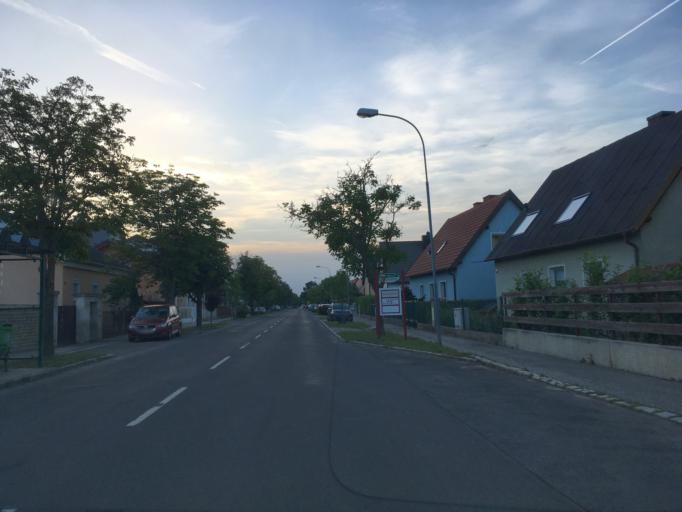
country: AT
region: Lower Austria
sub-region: Politischer Bezirk Baden
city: Teesdorf
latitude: 47.9451
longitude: 16.2877
